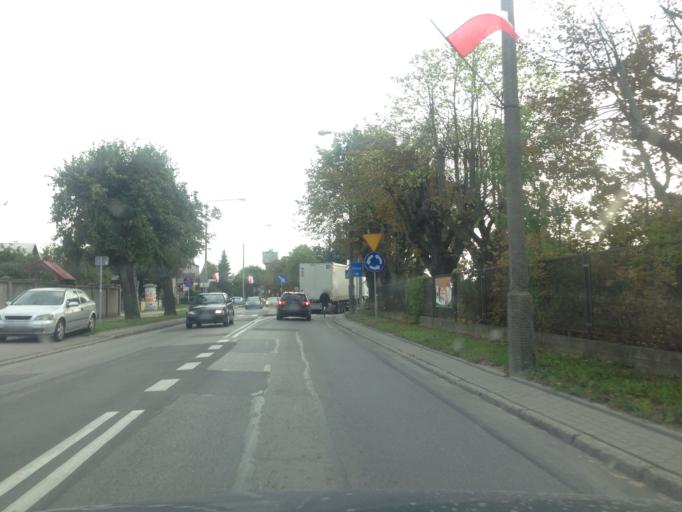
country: PL
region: Pomeranian Voivodeship
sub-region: Powiat kwidzynski
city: Kwidzyn
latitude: 53.7270
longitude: 18.9328
